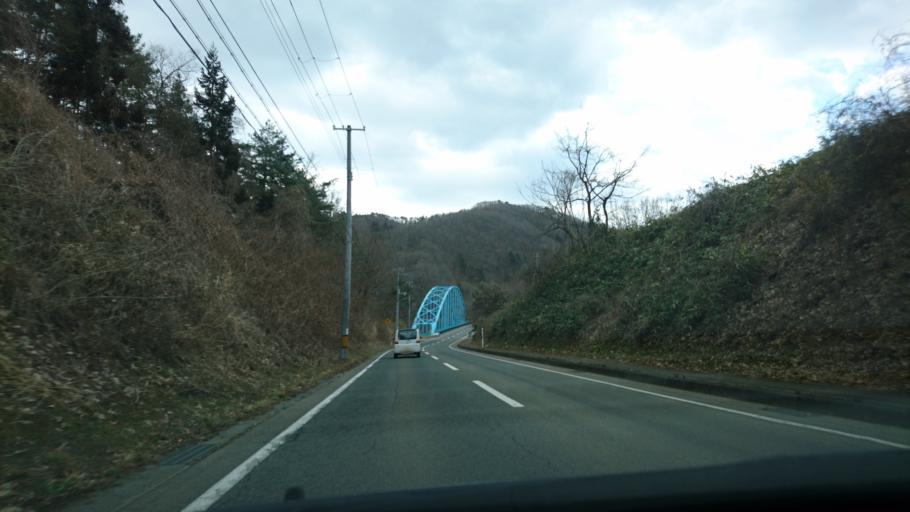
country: JP
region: Iwate
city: Shizukuishi
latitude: 39.6898
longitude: 141.0329
